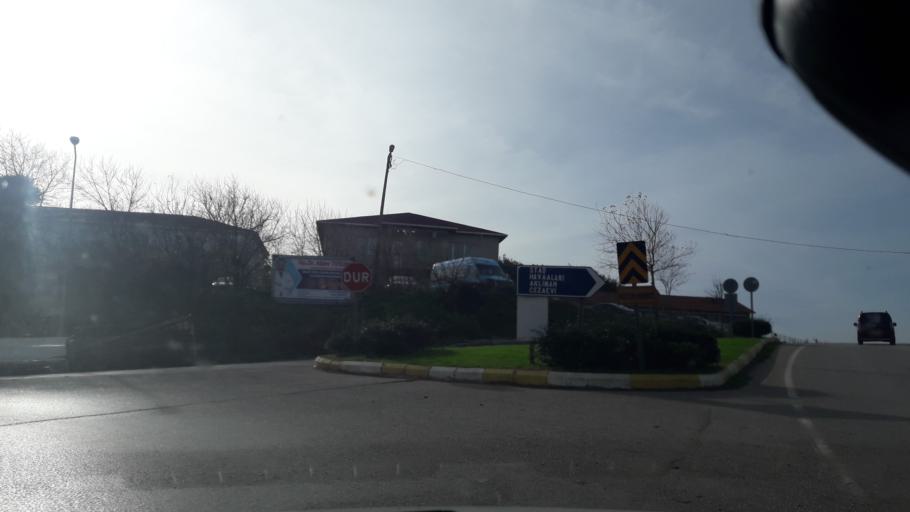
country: TR
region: Sinop
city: Sinop
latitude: 42.0246
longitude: 35.1384
